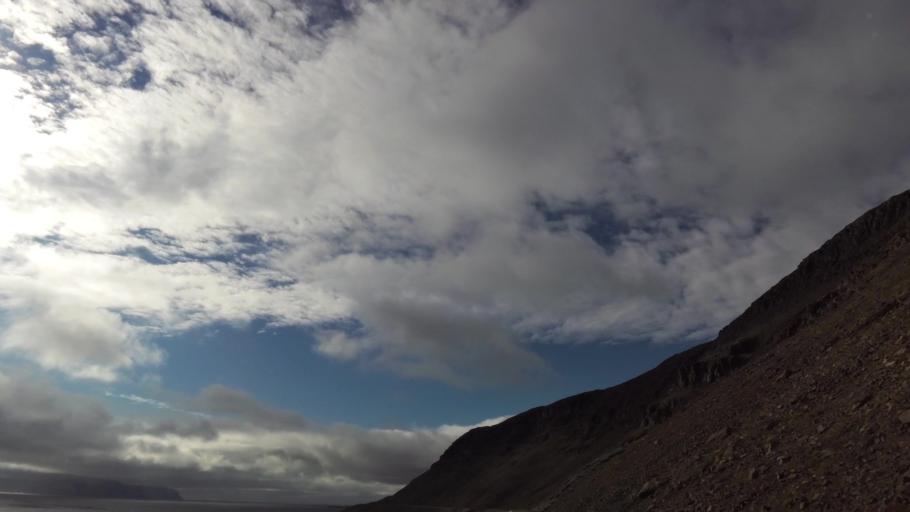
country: IS
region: West
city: Olafsvik
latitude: 65.5757
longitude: -23.9432
